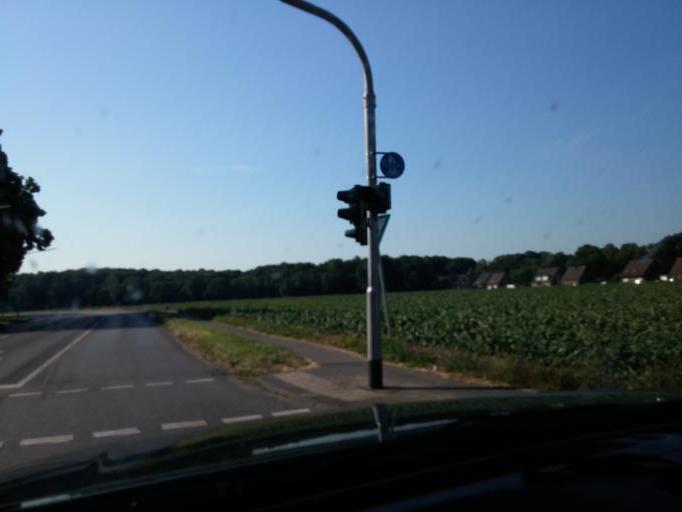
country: DE
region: North Rhine-Westphalia
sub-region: Regierungsbezirk Dusseldorf
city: Monchengladbach
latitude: 51.1345
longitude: 6.4037
